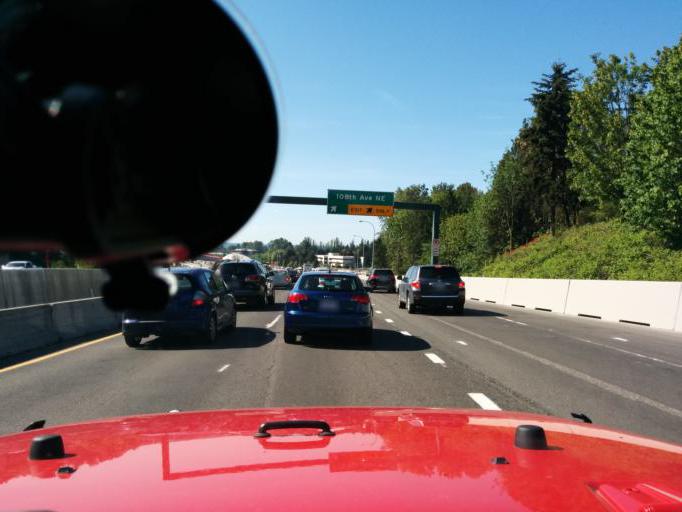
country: US
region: Washington
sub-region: King County
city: Clyde Hill
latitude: 47.6371
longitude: -122.1930
